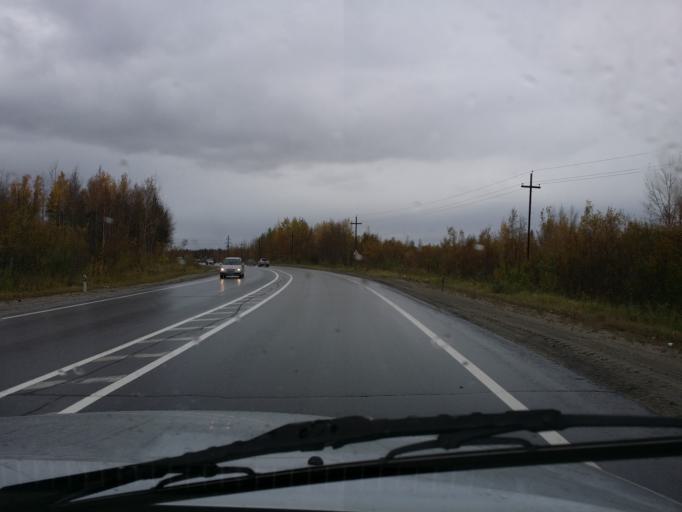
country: RU
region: Khanty-Mansiyskiy Avtonomnyy Okrug
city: Megion
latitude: 61.0853
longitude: 76.1149
